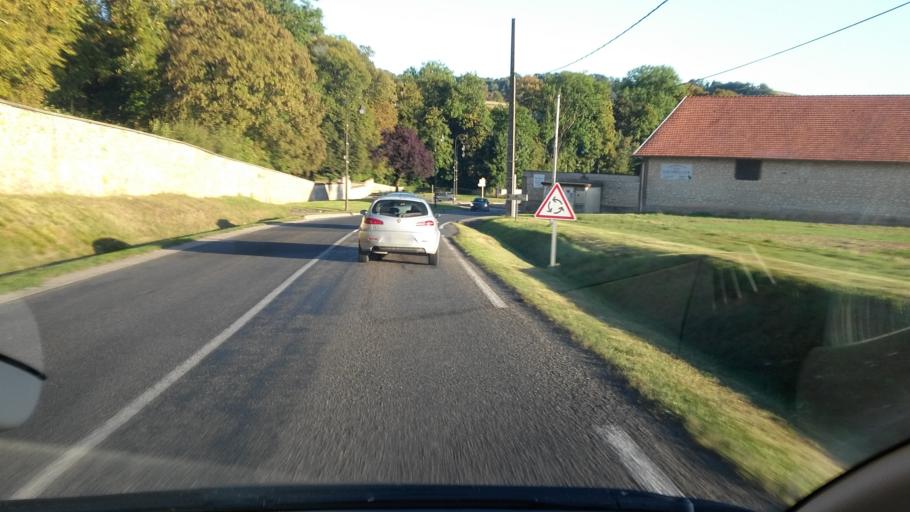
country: FR
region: Champagne-Ardenne
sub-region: Departement de la Marne
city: Tours-sur-Marne
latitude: 49.1045
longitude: 4.1161
